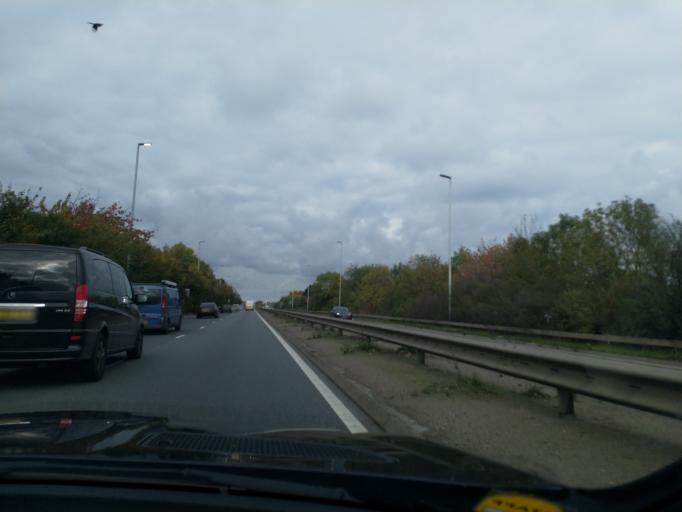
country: GB
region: England
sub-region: Greater London
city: Hayes
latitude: 51.5092
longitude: -0.4046
